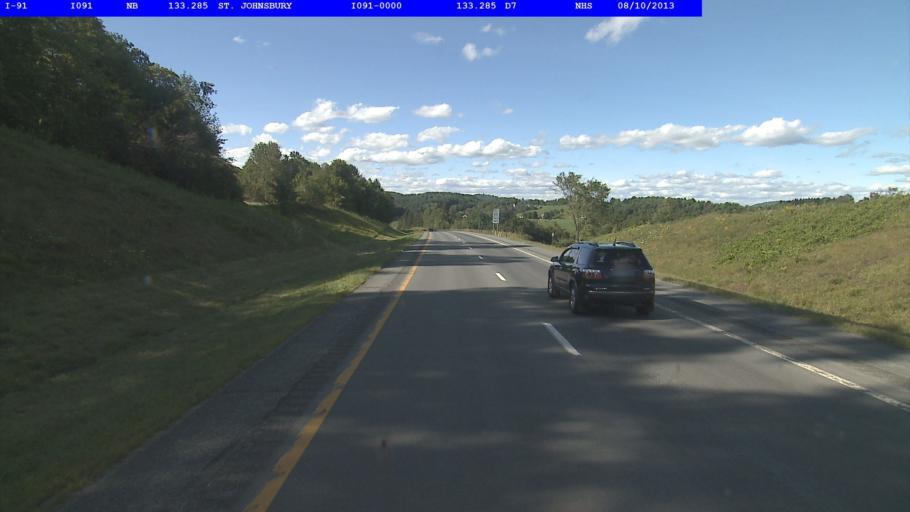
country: US
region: Vermont
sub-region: Caledonia County
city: St Johnsbury
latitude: 44.4643
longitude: -72.0233
